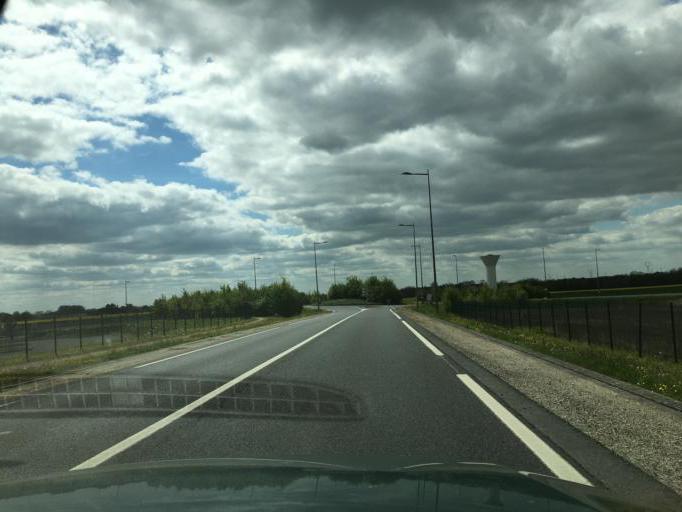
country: FR
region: Centre
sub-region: Departement du Loir-et-Cher
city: Mer
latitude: 47.7216
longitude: 1.5072
